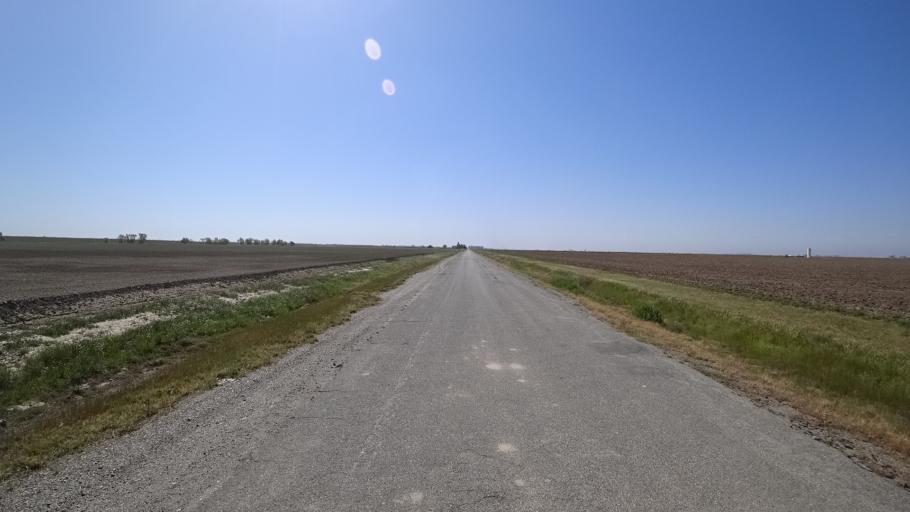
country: US
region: California
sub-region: Glenn County
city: Willows
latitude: 39.5214
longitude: -122.0373
